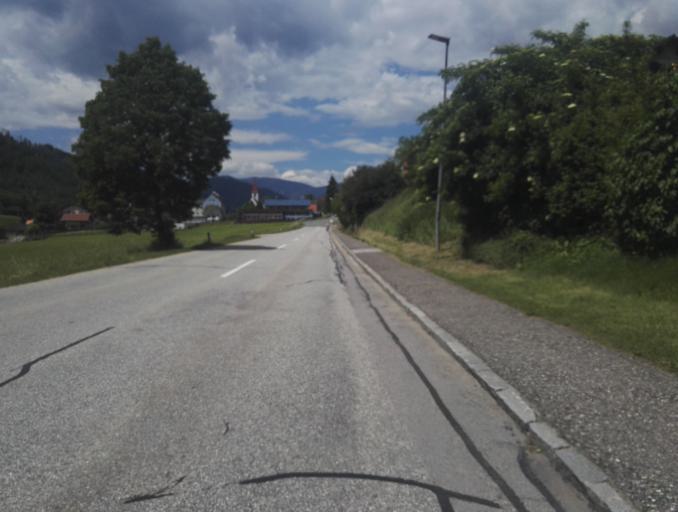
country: AT
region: Styria
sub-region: Politischer Bezirk Graz-Umgebung
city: Ubelbach
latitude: 47.2218
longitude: 15.2473
